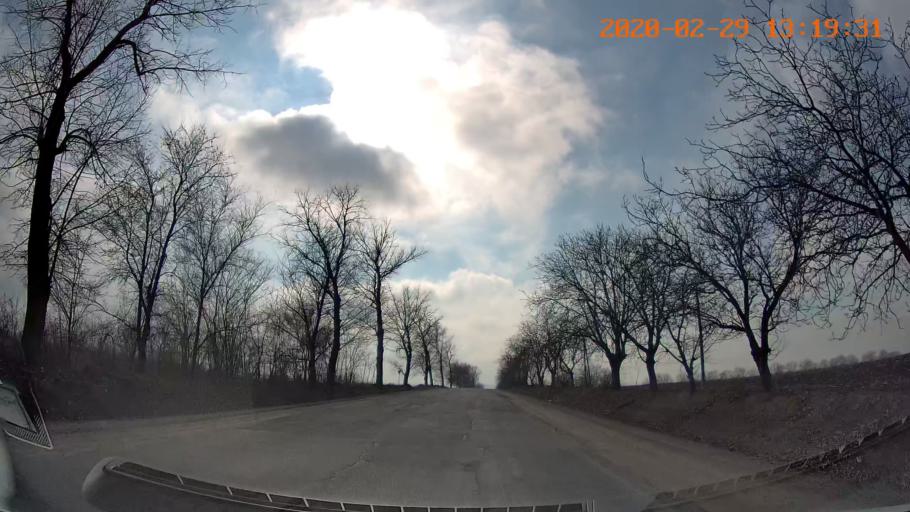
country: MD
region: Telenesti
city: Camenca
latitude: 47.9879
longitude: 28.6503
